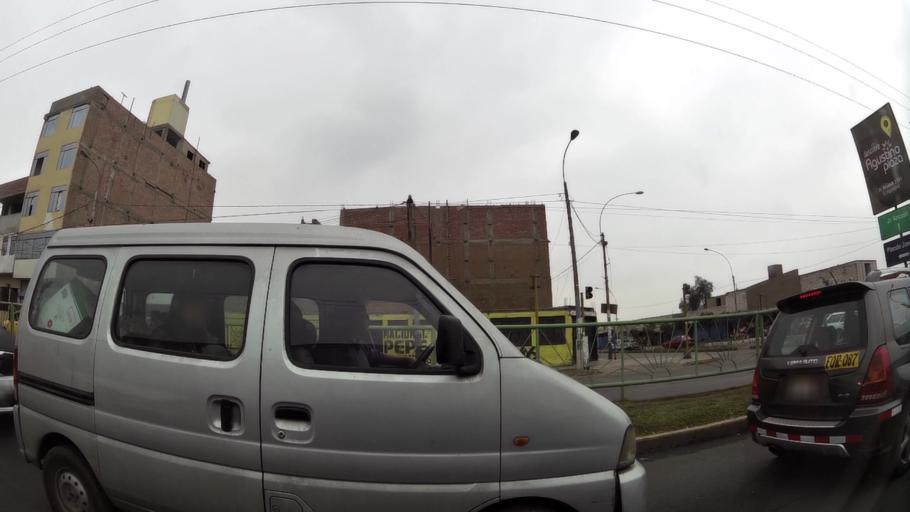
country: PE
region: Lima
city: Lima
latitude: -12.0416
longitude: -77.0045
